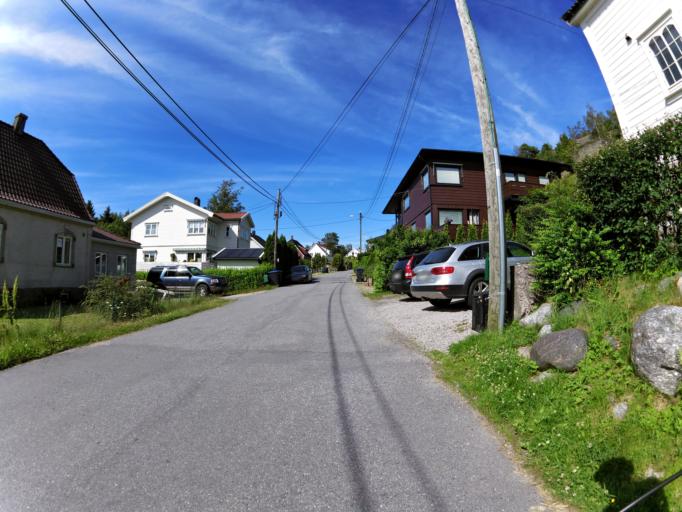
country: NO
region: Ostfold
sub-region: Fredrikstad
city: Fredrikstad
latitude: 59.2236
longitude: 10.9406
